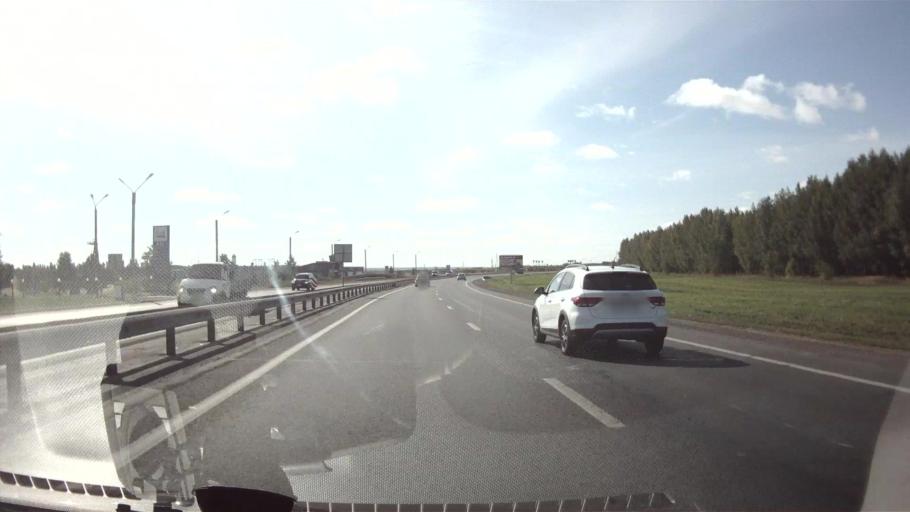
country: RU
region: Ulyanovsk
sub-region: Ulyanovskiy Rayon
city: Ulyanovsk
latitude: 54.2750
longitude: 48.2607
